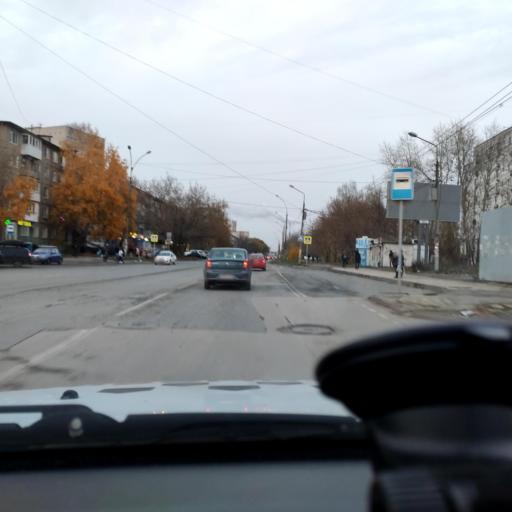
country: RU
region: Perm
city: Perm
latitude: 57.9716
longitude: 56.2320
